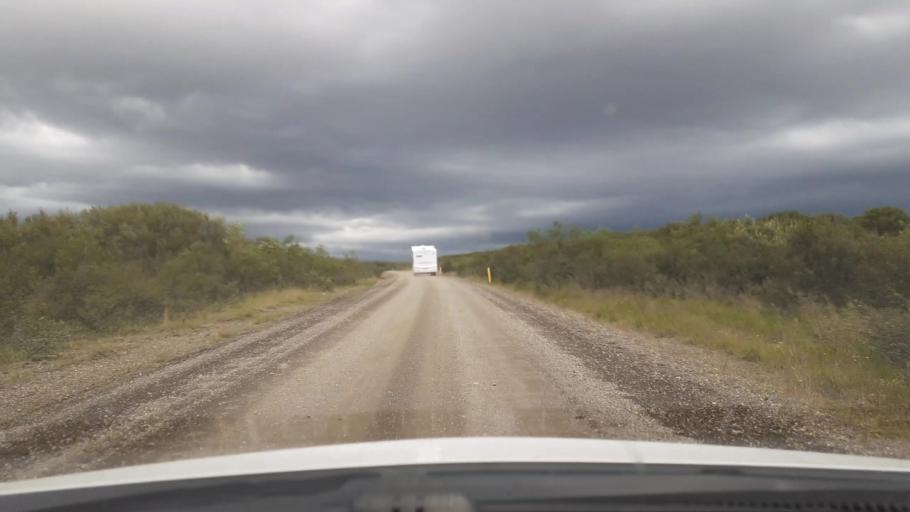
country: IS
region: West
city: Borgarnes
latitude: 64.5481
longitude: -21.6196
